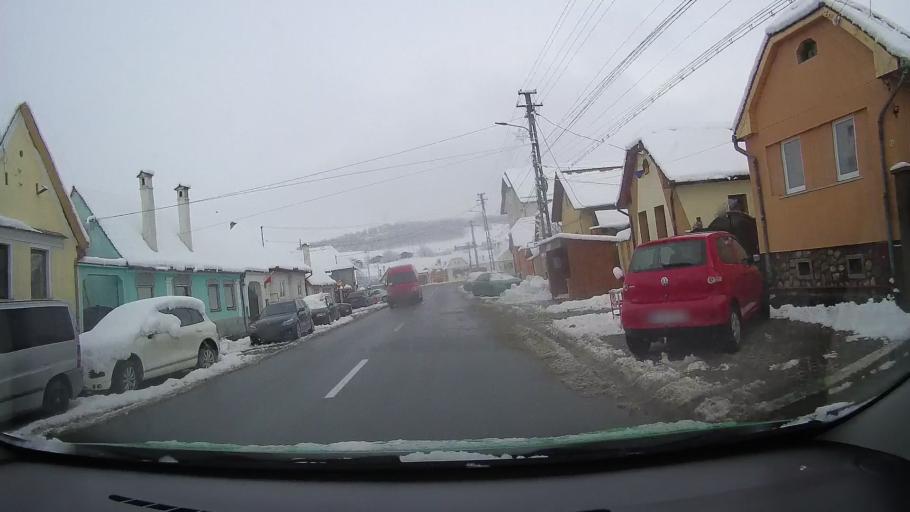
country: RO
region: Sibiu
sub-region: Comuna Cristian
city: Cristian
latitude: 45.7879
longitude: 24.0308
